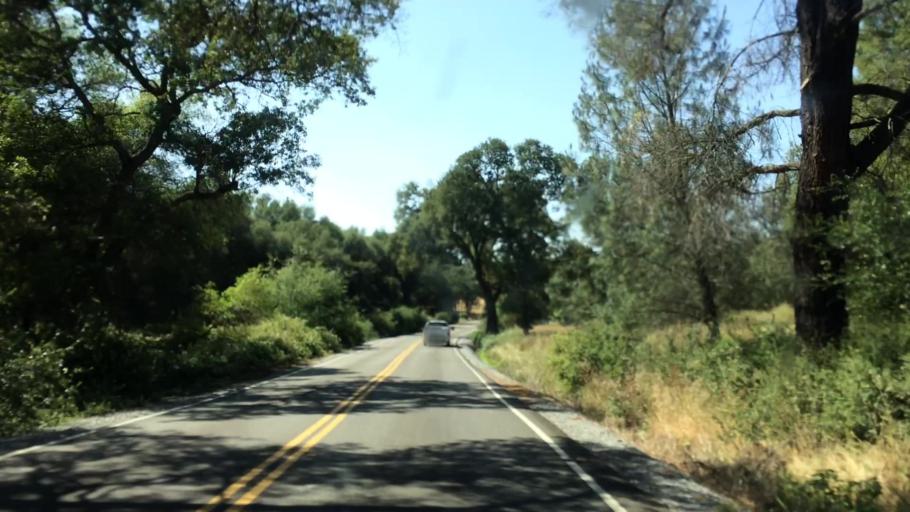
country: US
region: California
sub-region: Amador County
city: Plymouth
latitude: 38.5083
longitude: -120.9460
